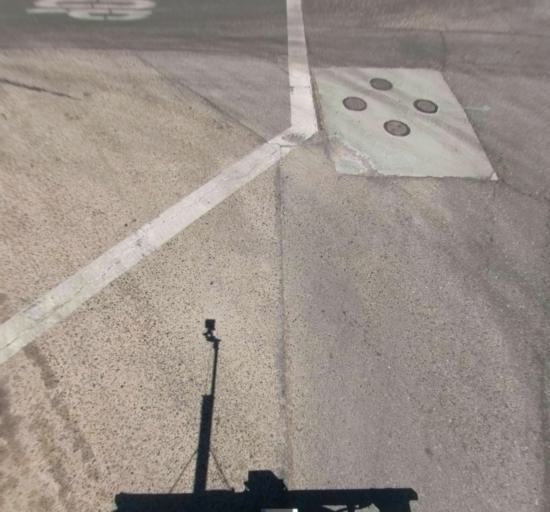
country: US
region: California
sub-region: Madera County
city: Madera Acres
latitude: 36.9966
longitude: -120.1063
